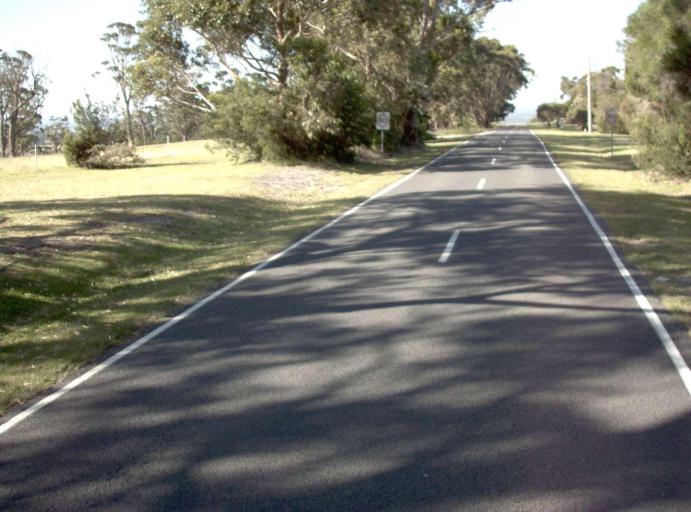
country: AU
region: Victoria
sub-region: East Gippsland
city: Lakes Entrance
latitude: -37.7902
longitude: 148.5357
